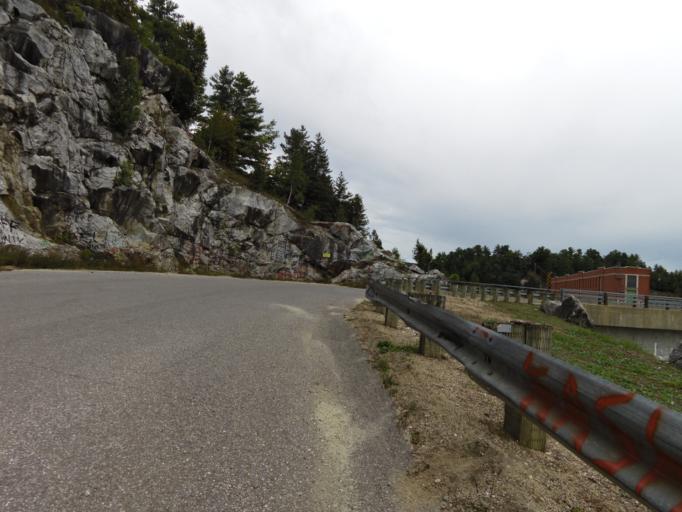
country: CA
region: Quebec
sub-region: Outaouais
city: Wakefield
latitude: 45.8110
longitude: -75.9334
